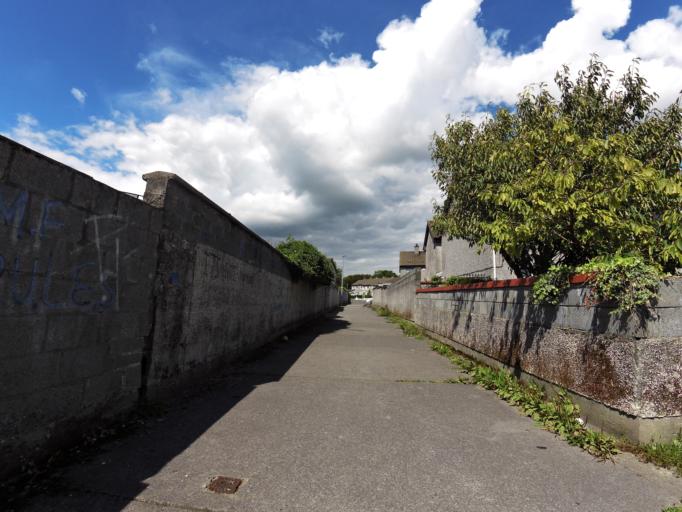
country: IE
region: Connaught
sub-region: County Galway
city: Gaillimh
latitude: 53.2782
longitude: -9.0761
